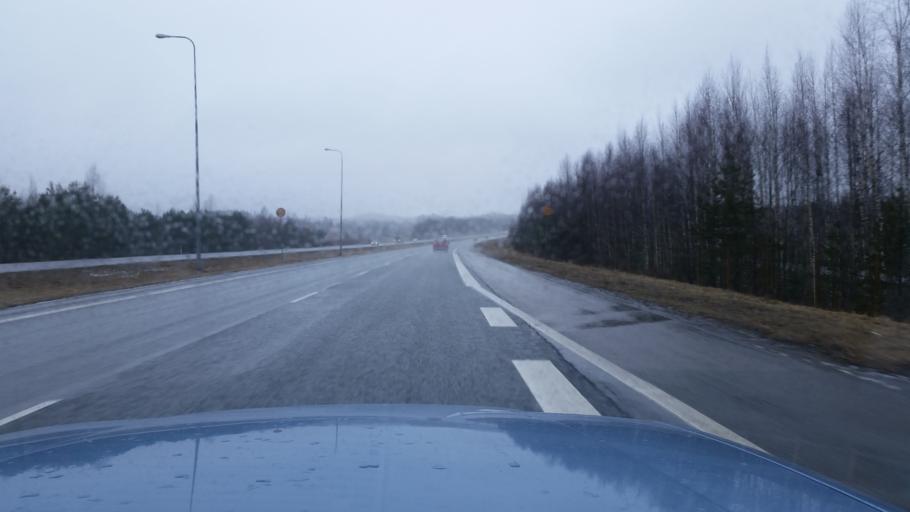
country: FI
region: Haeme
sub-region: Haemeenlinna
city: Janakkala
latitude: 60.8599
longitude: 24.5886
